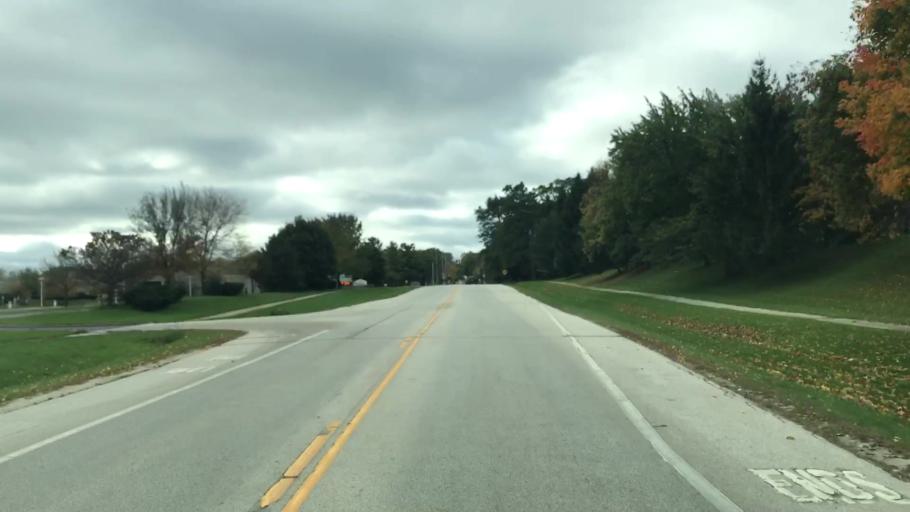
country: US
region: Wisconsin
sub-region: Waukesha County
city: Brookfield
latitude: 43.0715
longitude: -88.1259
